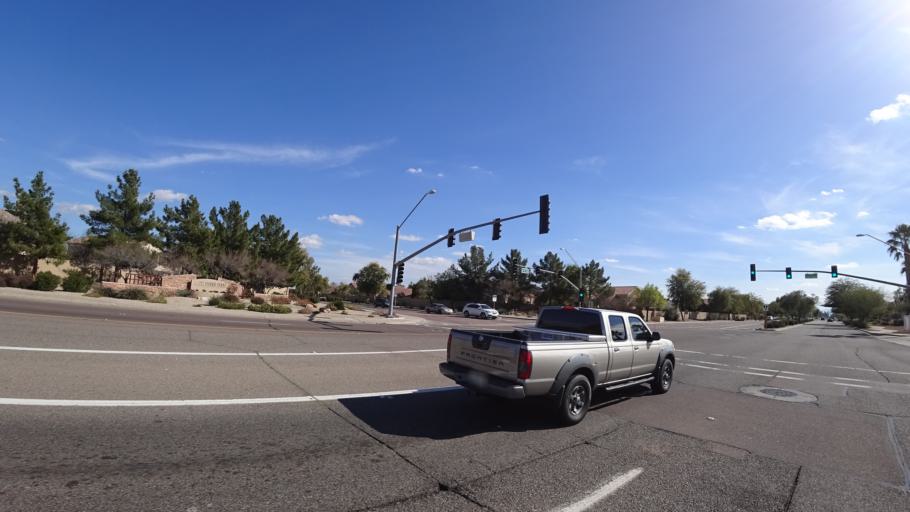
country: US
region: Arizona
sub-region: Maricopa County
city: Sun City
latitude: 33.6748
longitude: -112.2205
